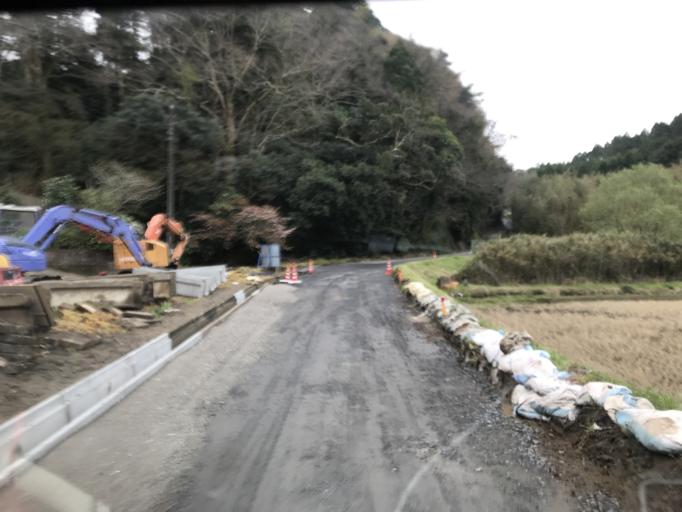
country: JP
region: Chiba
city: Sawara
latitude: 35.8638
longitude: 140.5136
